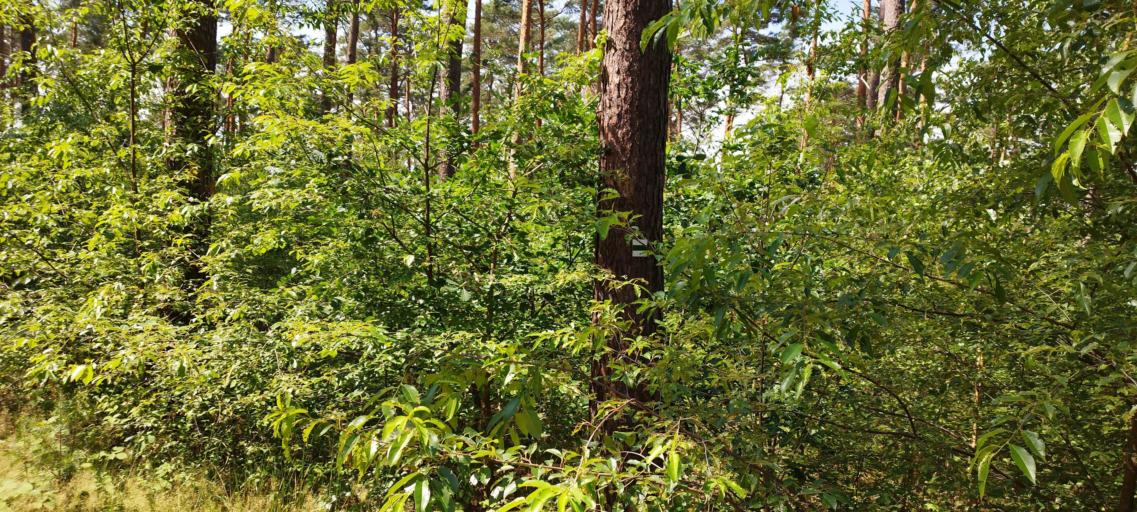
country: DE
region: Brandenburg
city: Langewahl
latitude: 52.3133
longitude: 14.1007
